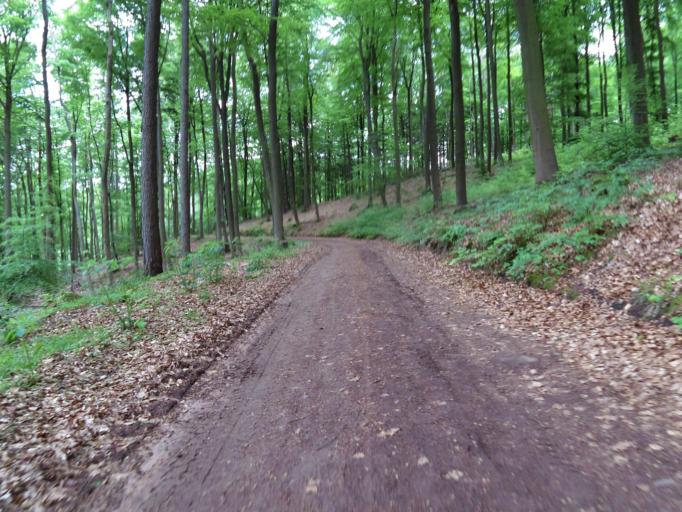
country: DE
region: Rheinland-Pfalz
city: Neidenfels
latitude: 49.4118
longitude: 8.0595
